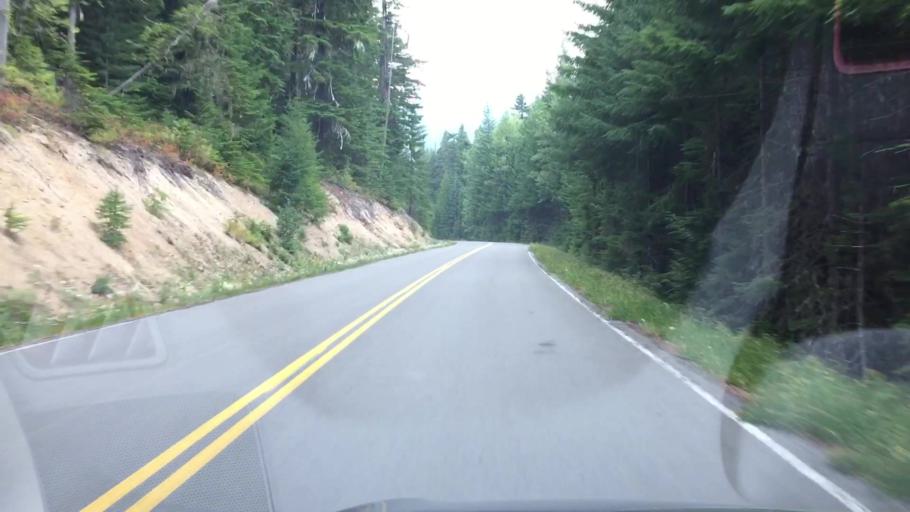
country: US
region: Washington
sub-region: Klickitat County
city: White Salmon
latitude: 46.1198
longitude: -121.6216
